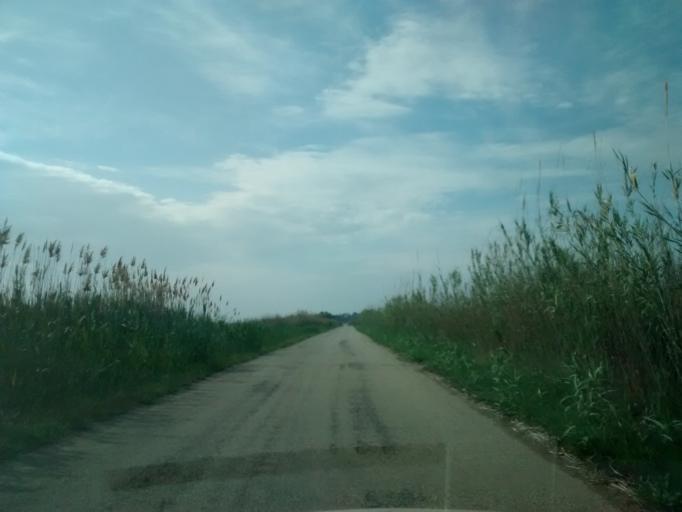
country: ES
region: Catalonia
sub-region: Provincia de Tarragona
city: Deltebre
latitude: 40.6911
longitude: 0.8436
